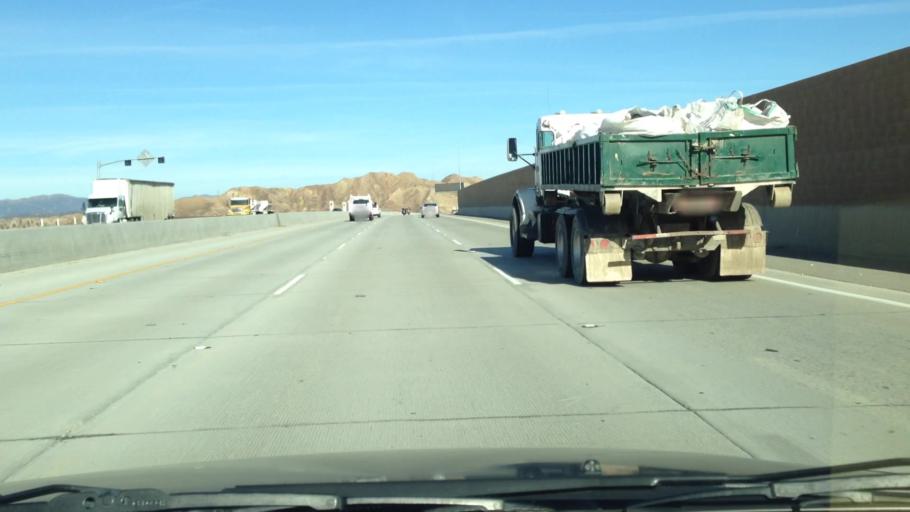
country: US
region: California
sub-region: Los Angeles County
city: Valencia
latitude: 34.4334
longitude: -118.6203
